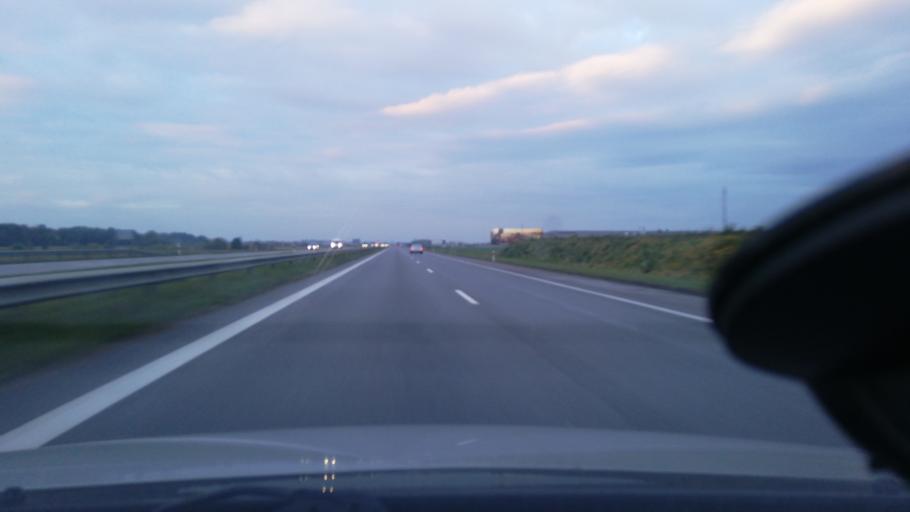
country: LT
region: Klaipedos apskritis
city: Gargzdai
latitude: 55.7173
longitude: 21.2865
